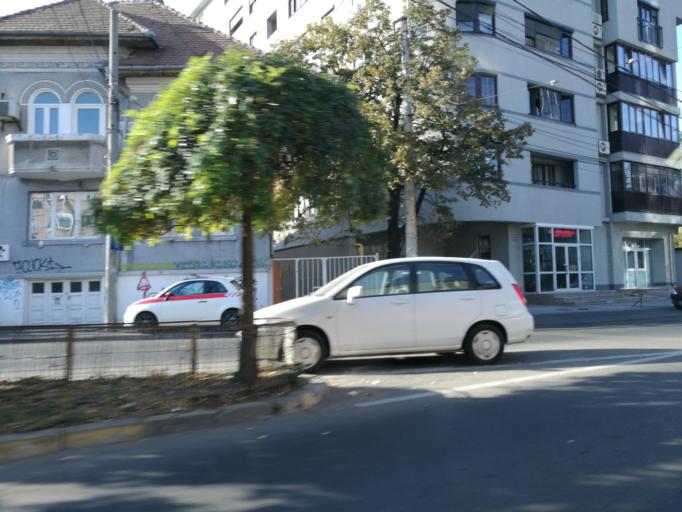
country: RO
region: Bucuresti
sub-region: Municipiul Bucuresti
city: Bucharest
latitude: 44.4419
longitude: 26.1204
